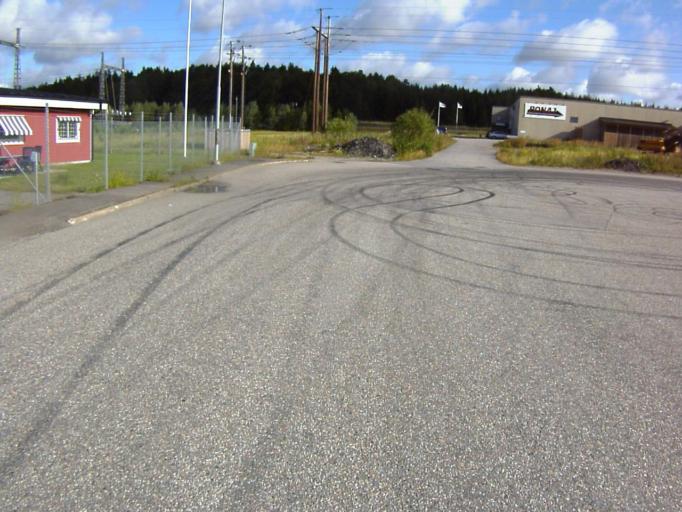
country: SE
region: Soedermanland
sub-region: Eskilstuna Kommun
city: Eskilstuna
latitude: 59.3776
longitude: 16.5749
